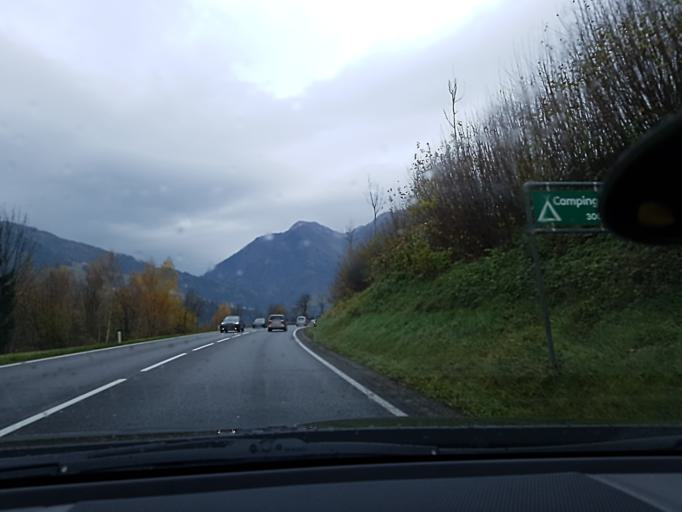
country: AT
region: Salzburg
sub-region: Politischer Bezirk Sankt Johann im Pongau
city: Sankt Johann im Pongau
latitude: 47.3479
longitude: 13.1939
